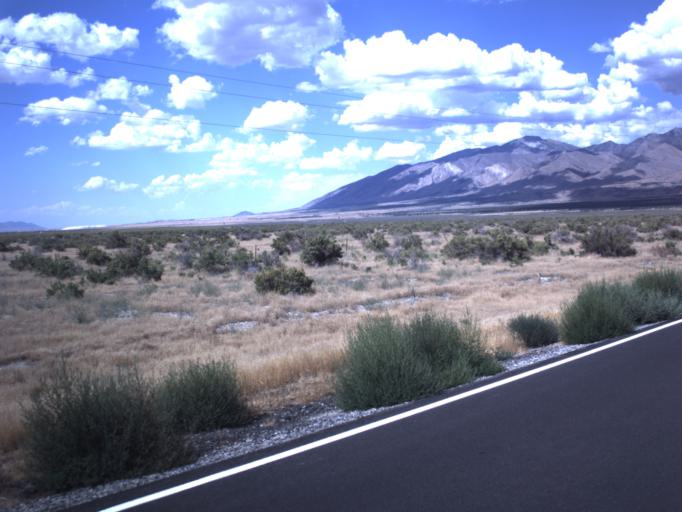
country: US
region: Utah
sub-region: Tooele County
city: Grantsville
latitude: 40.2611
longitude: -112.6918
